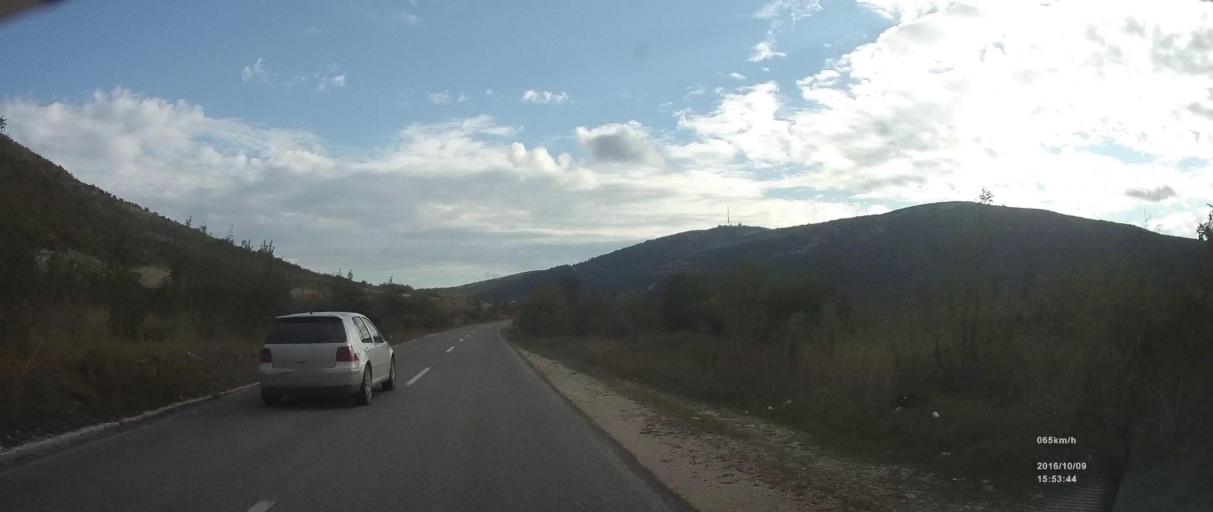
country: HR
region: Splitsko-Dalmatinska
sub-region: Grad Trogir
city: Trogir
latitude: 43.6024
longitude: 16.2248
